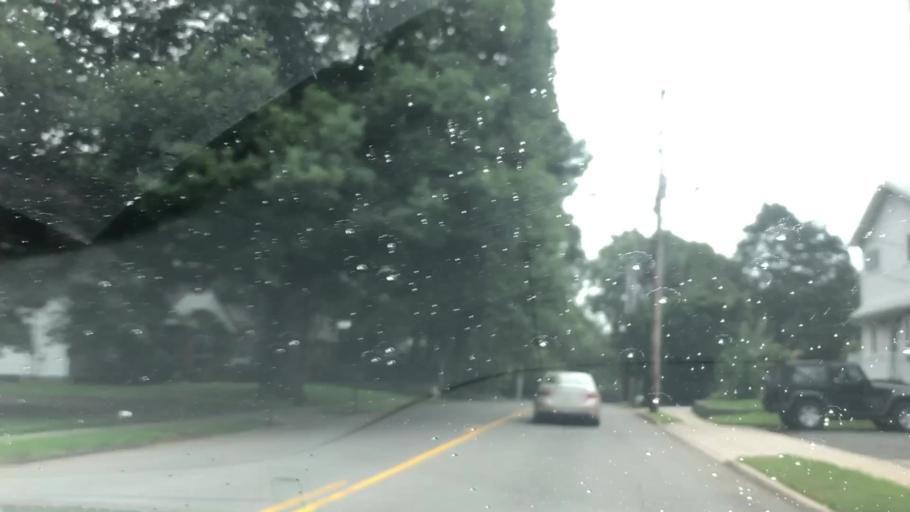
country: US
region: New Jersey
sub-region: Essex County
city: Upper Montclair
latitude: 40.8571
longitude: -74.1897
